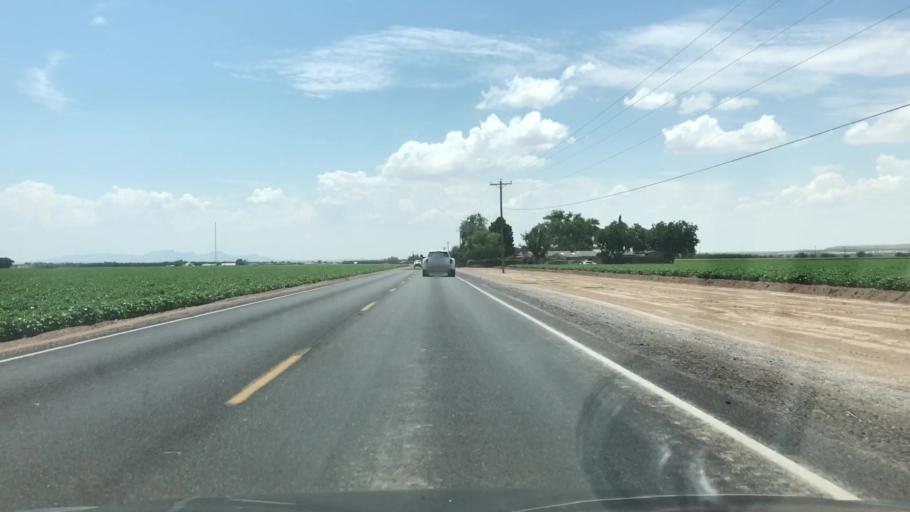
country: US
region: New Mexico
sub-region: Dona Ana County
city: La Union
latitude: 31.9795
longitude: -106.6515
